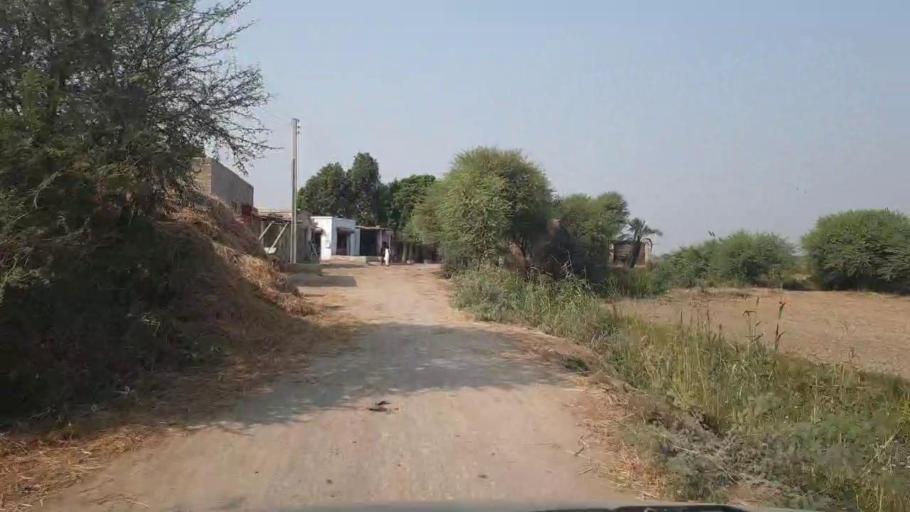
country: PK
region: Sindh
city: Tando Muhammad Khan
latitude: 25.0537
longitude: 68.3666
